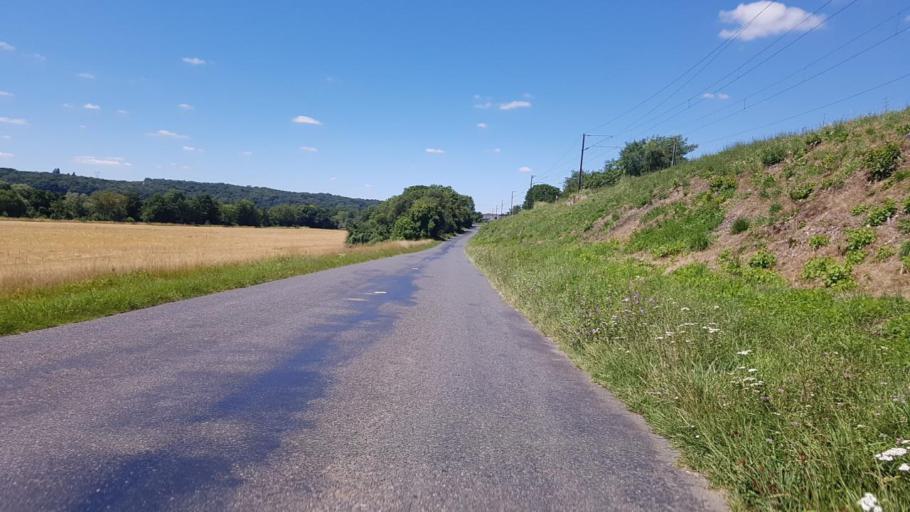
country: FR
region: Ile-de-France
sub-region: Departement de Seine-et-Marne
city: Changis-sur-Marne
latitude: 48.9592
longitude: 3.0374
